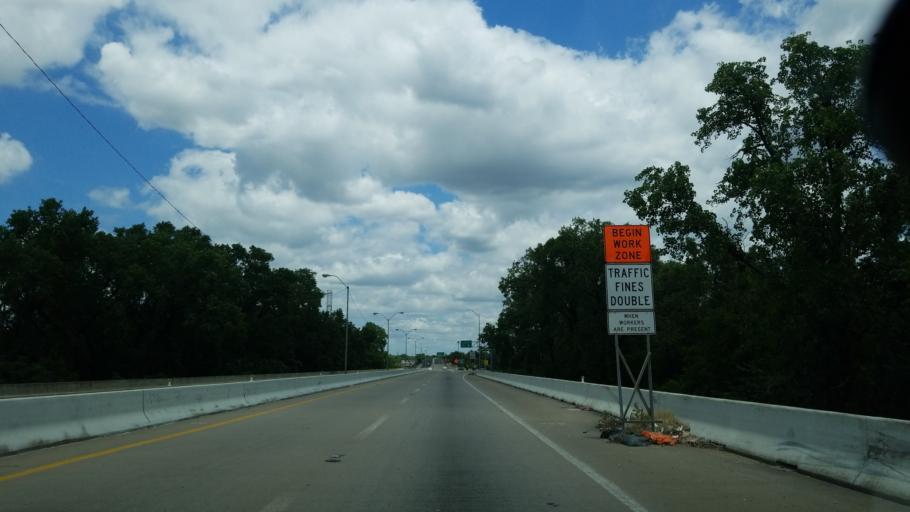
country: US
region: Texas
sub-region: Dallas County
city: Dallas
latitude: 32.7294
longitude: -96.7580
